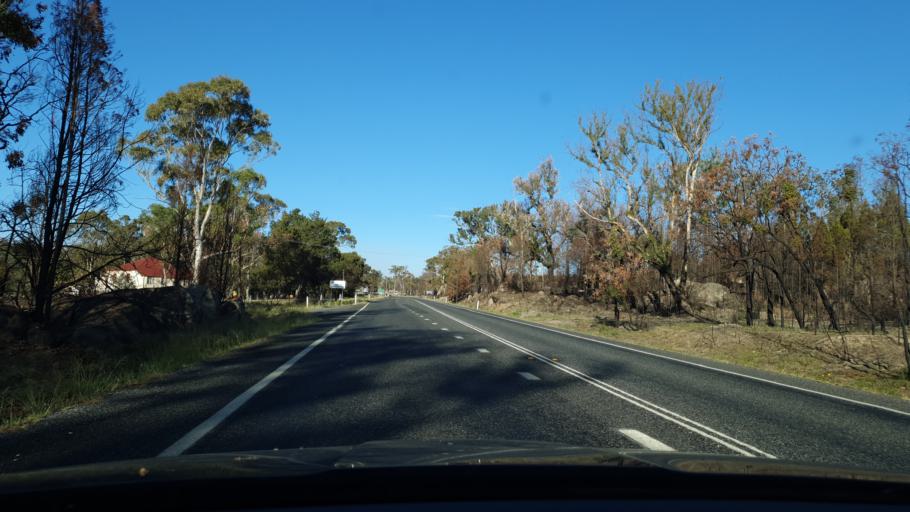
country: AU
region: Queensland
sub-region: Southern Downs
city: Stanthorpe
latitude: -28.6383
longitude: 151.9456
